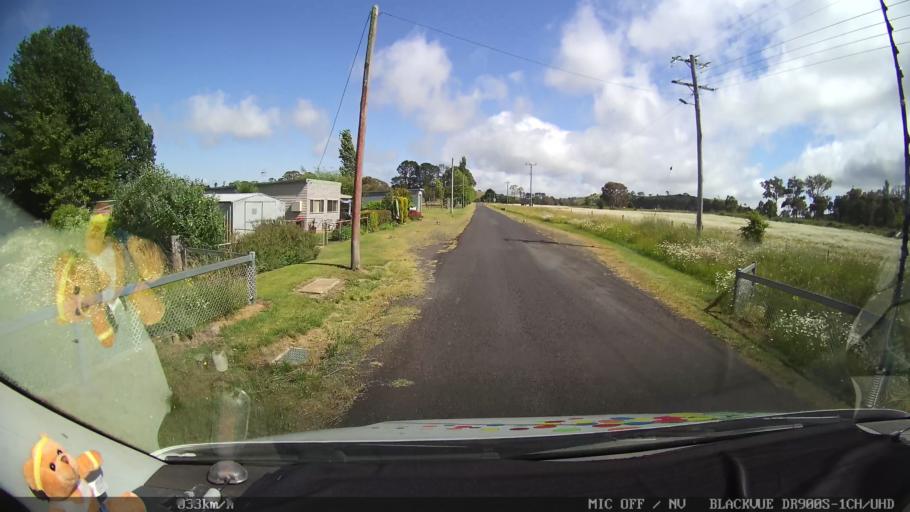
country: AU
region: New South Wales
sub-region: Guyra
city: Guyra
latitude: -30.0195
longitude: 151.6587
